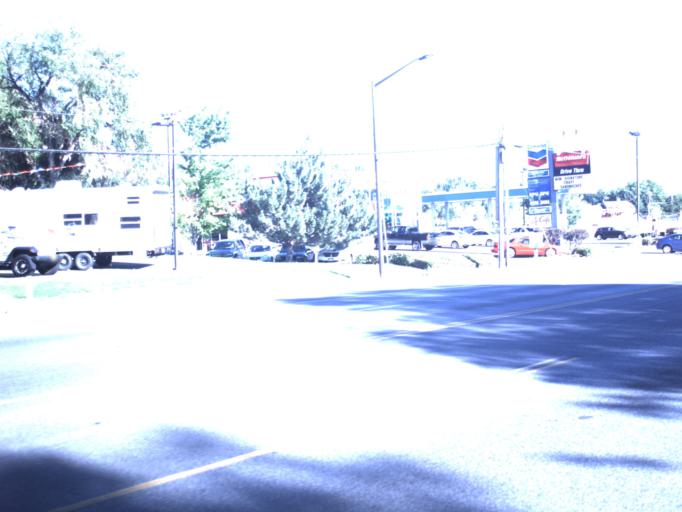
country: US
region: Utah
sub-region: Utah County
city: Springville
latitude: 40.1868
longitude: -111.6108
